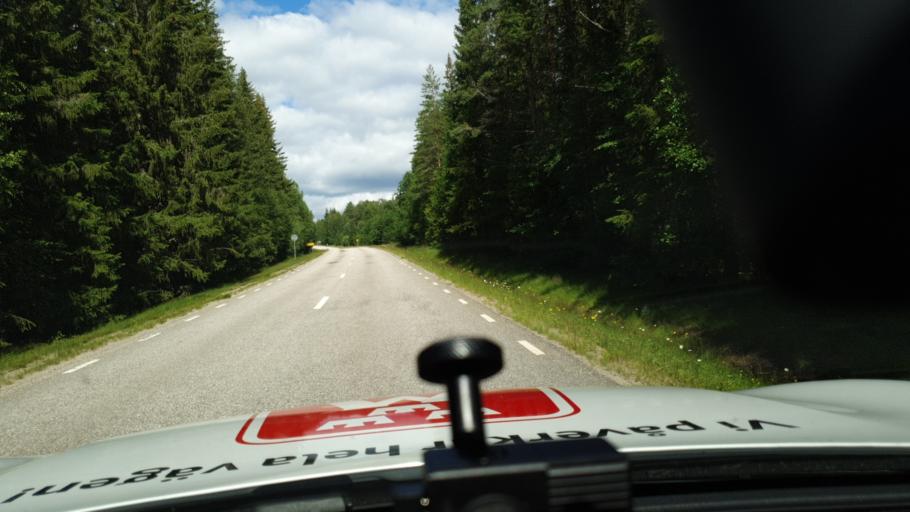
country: NO
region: Hedmark
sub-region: Trysil
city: Innbygda
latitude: 60.9655
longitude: 12.4829
